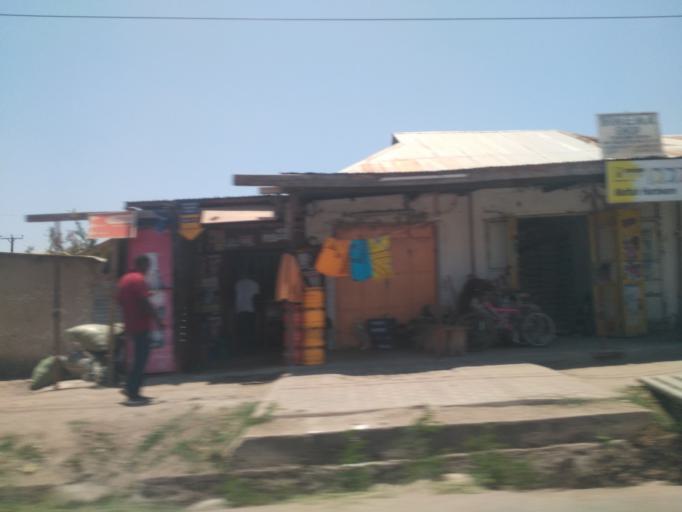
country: TZ
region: Dodoma
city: Dodoma
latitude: -6.1745
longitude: 35.7430
